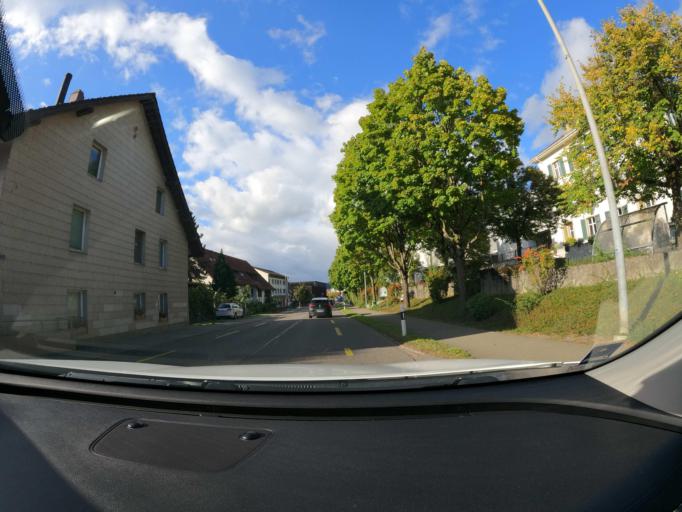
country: CH
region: Aargau
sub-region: Bezirk Brugg
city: Hausen
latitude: 47.4628
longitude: 8.2116
